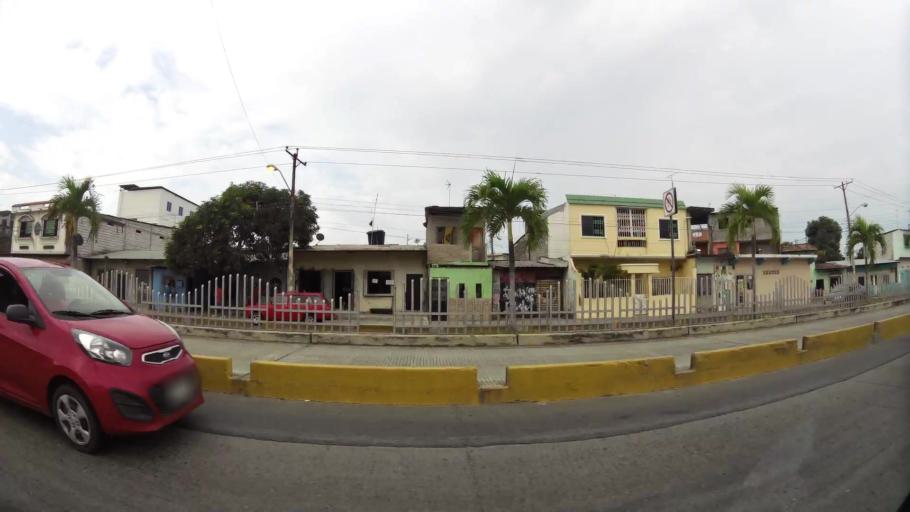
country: EC
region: Guayas
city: Guayaquil
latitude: -2.2582
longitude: -79.8792
